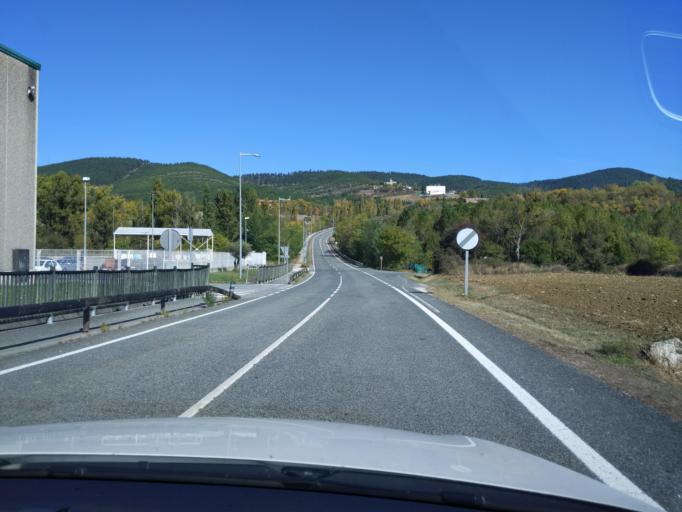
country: ES
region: Navarre
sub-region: Provincia de Navarra
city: Egues-Uharte
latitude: 42.8294
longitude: -1.5731
